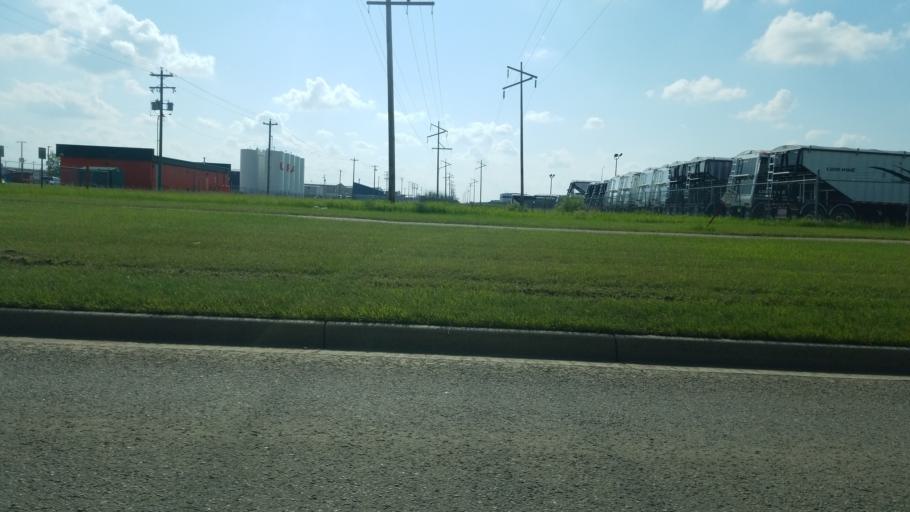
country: CA
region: Saskatchewan
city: Lloydminster
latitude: 53.2925
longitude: -110.0342
